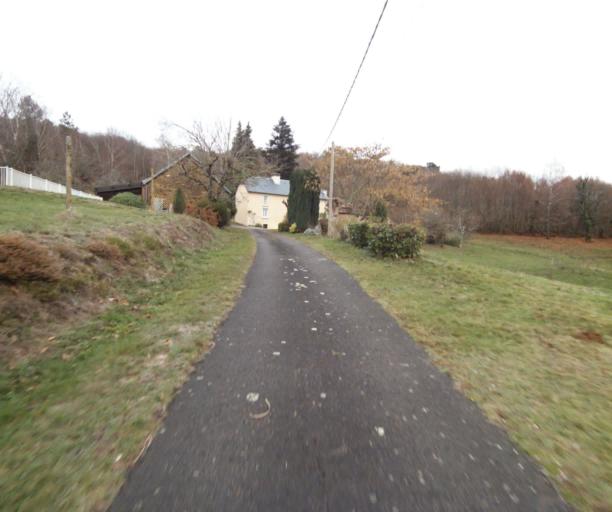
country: FR
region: Limousin
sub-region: Departement de la Correze
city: Cornil
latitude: 45.2291
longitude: 1.6577
